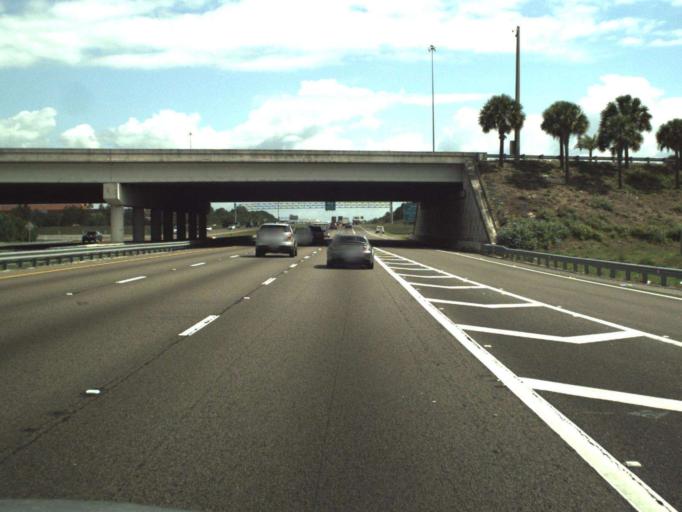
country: US
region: Florida
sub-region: Seminole County
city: Heathrow
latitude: 28.7553
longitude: -81.3634
